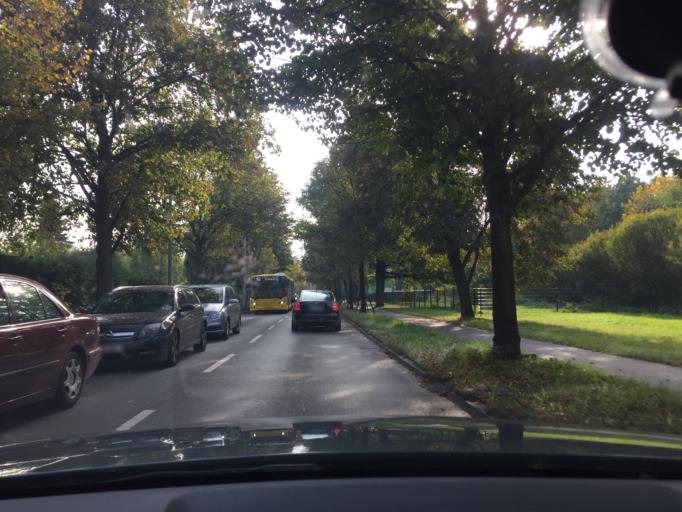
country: DE
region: Berlin
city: Buch
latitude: 52.6325
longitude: 13.5002
